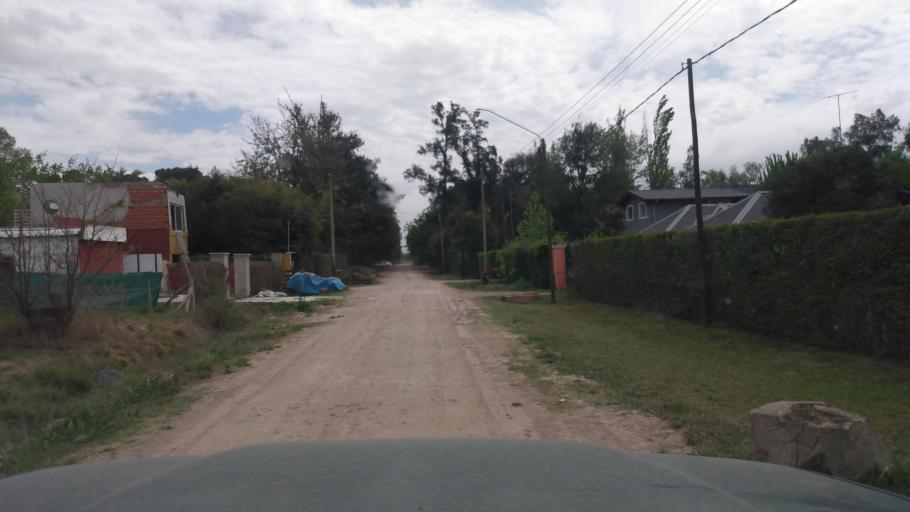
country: AR
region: Buenos Aires
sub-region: Partido de Lujan
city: Lujan
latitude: -34.5909
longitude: -59.1328
